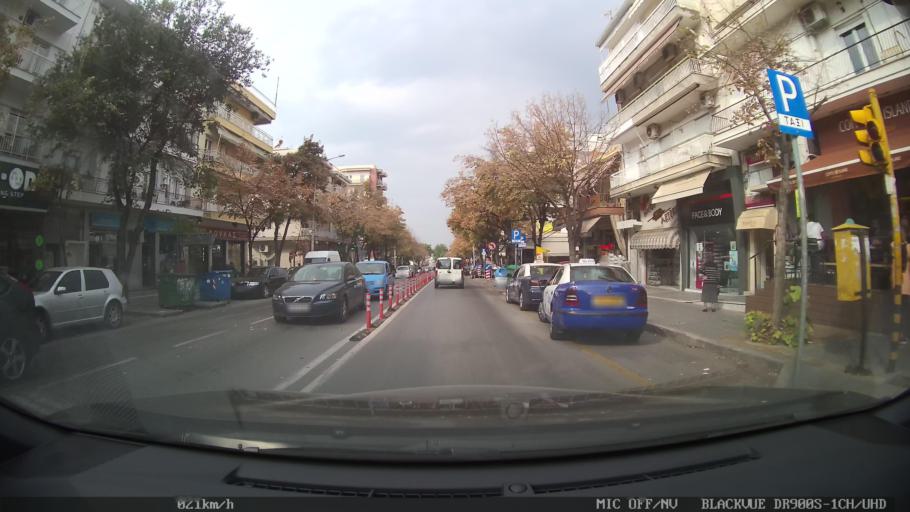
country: GR
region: Central Macedonia
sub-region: Nomos Thessalonikis
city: Triandria
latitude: 40.6152
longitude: 22.9763
